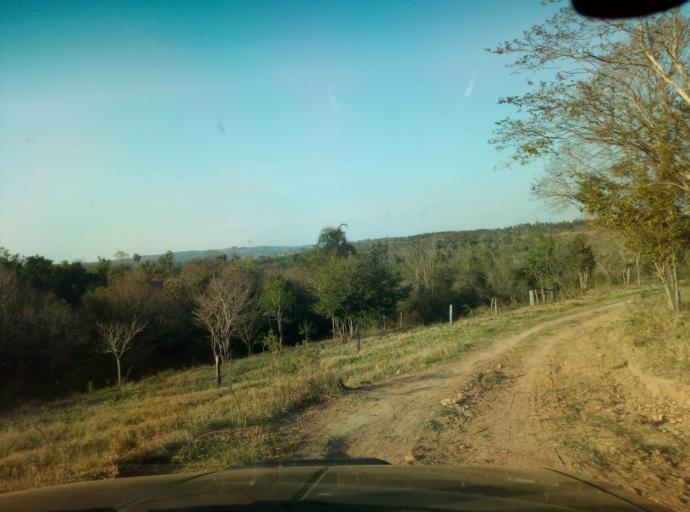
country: PY
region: Caaguazu
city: Doctor Cecilio Baez
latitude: -25.2001
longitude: -56.1288
